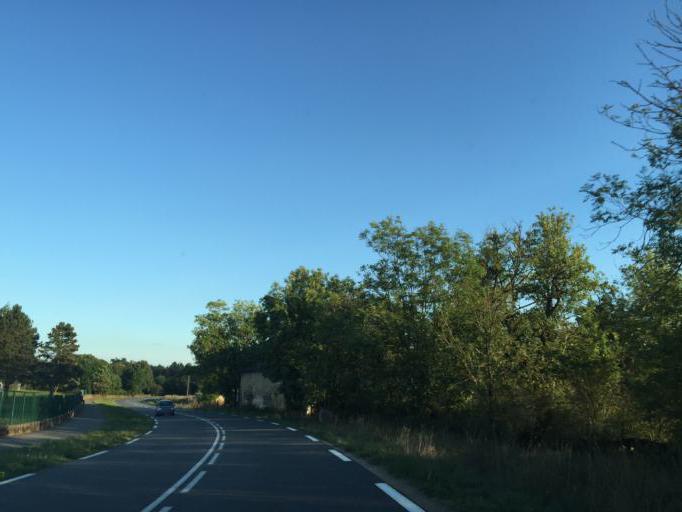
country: FR
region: Midi-Pyrenees
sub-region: Departement de l'Aveyron
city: Sebazac-Concoures
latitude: 44.3991
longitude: 2.5605
